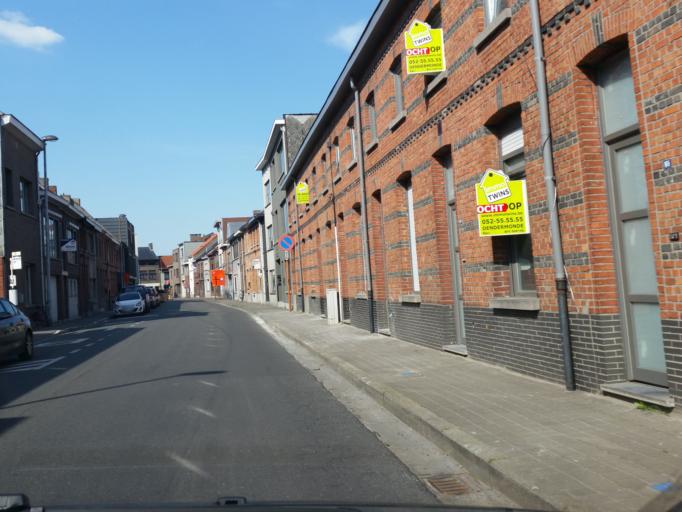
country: BE
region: Flanders
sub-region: Provincie Oost-Vlaanderen
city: Sint-Niklaas
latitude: 51.1749
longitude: 4.1417
